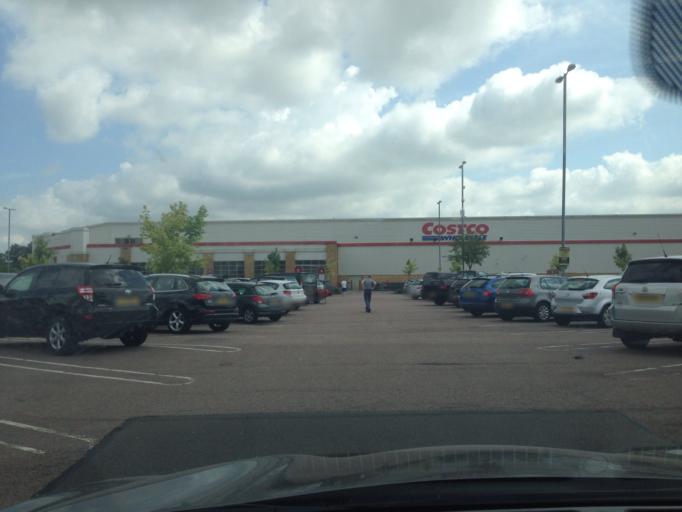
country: GB
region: England
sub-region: Hertfordshire
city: Bushey
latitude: 51.6628
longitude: -0.3628
